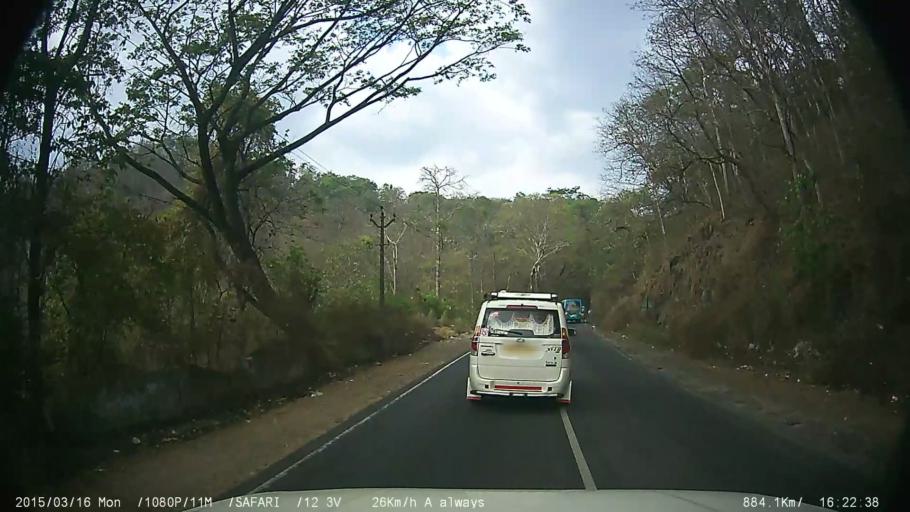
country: IN
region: Kerala
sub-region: Thrissur District
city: Chelakara
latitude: 10.5749
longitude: 76.3785
